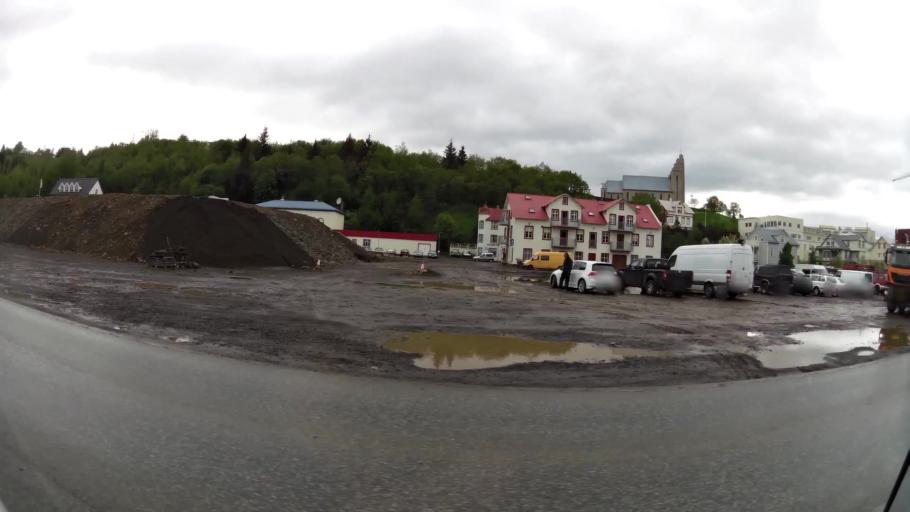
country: IS
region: Northeast
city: Akureyri
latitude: 65.6790
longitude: -18.0876
